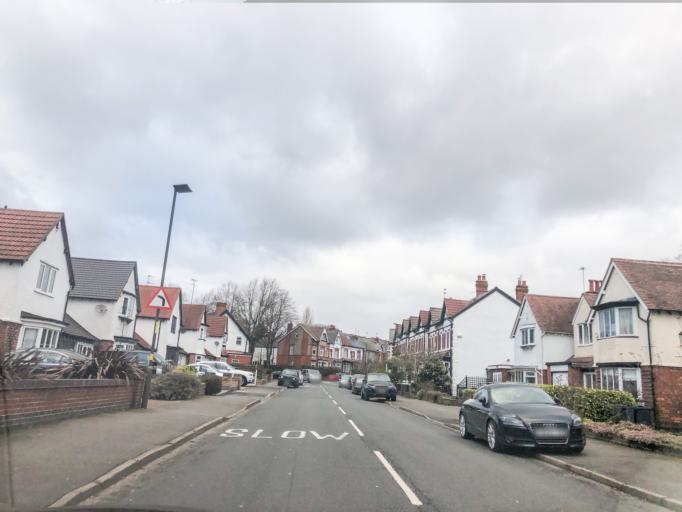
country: GB
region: England
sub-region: City and Borough of Birmingham
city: Birmingham
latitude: 52.4292
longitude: -1.8952
